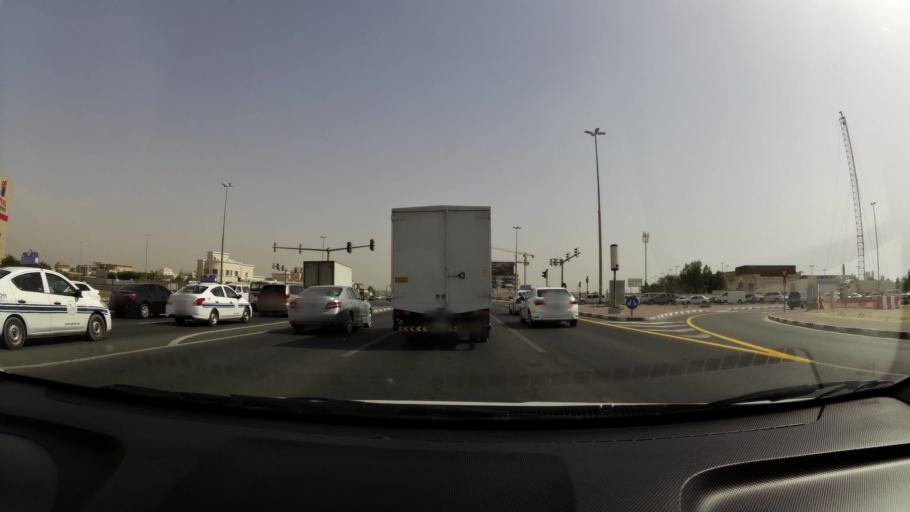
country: AE
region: Ash Shariqah
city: Sharjah
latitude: 25.2815
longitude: 55.3968
